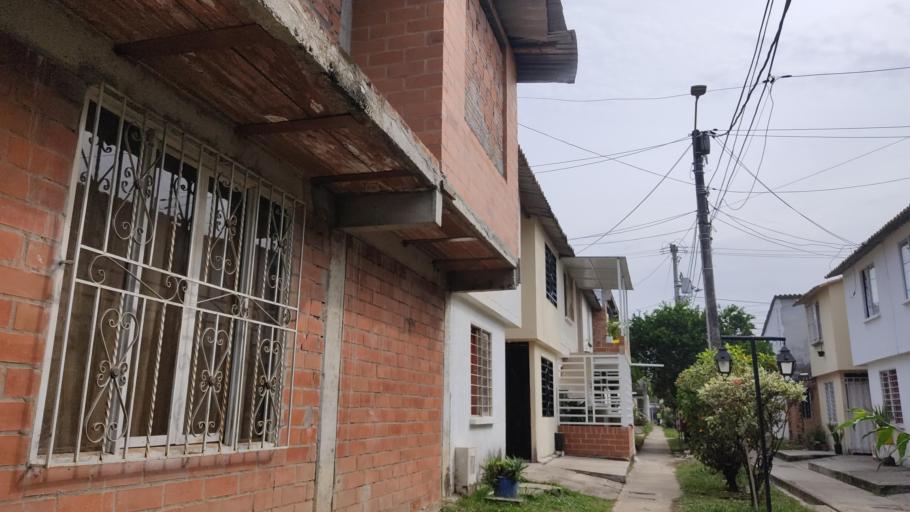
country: CO
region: Valle del Cauca
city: Jamundi
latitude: 3.2384
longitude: -76.5110
